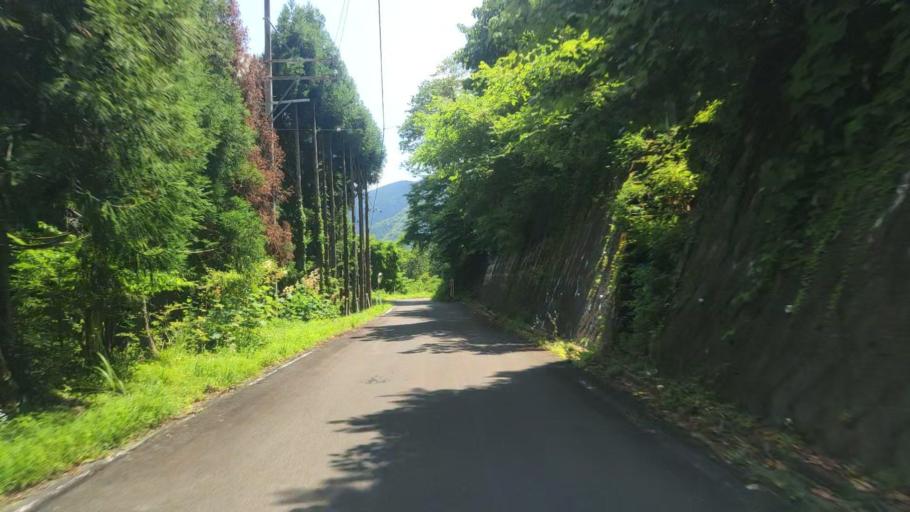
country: JP
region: Fukui
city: Ono
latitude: 35.7373
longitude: 136.5800
